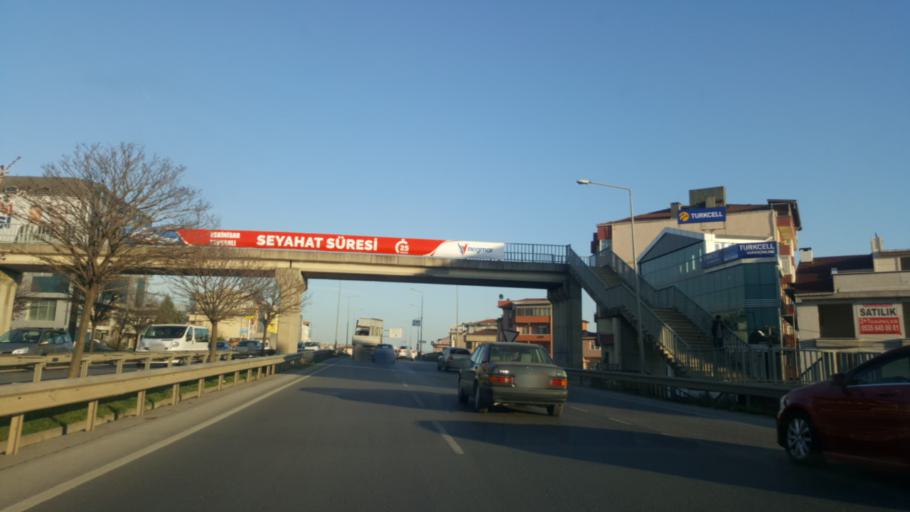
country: TR
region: Kocaeli
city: Darica
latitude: 40.7878
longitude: 29.4115
